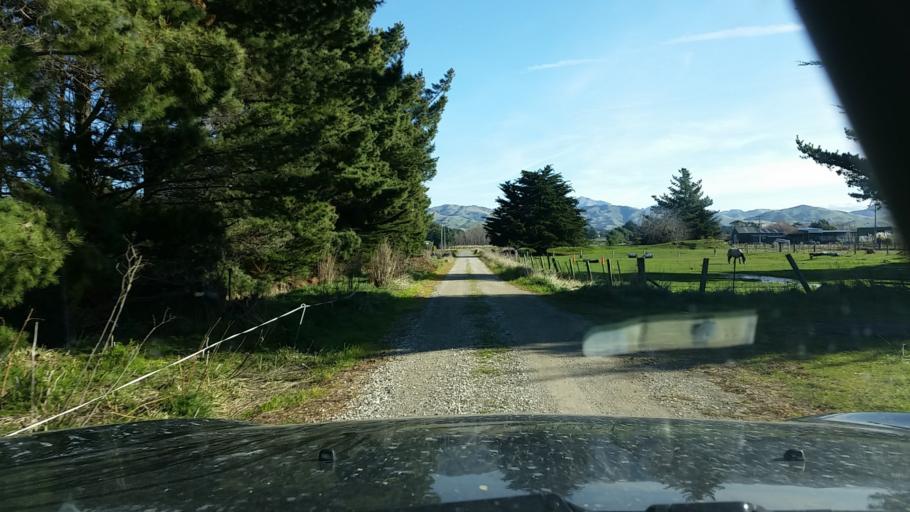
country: NZ
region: Marlborough
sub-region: Marlborough District
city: Blenheim
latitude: -41.8275
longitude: 174.1519
